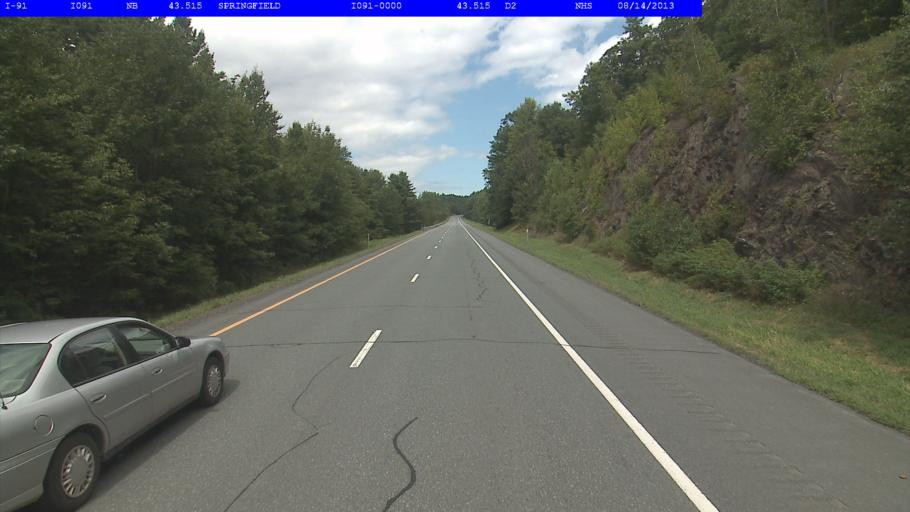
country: US
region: New Hampshire
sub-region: Sullivan County
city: Charlestown
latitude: 43.2917
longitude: -72.4270
